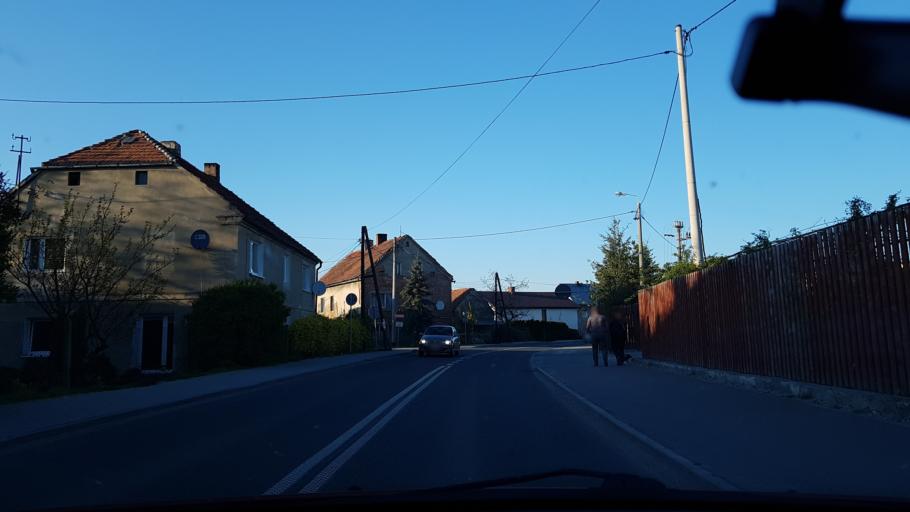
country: PL
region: Opole Voivodeship
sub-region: Powiat nyski
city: Nysa
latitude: 50.4353
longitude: 17.3055
